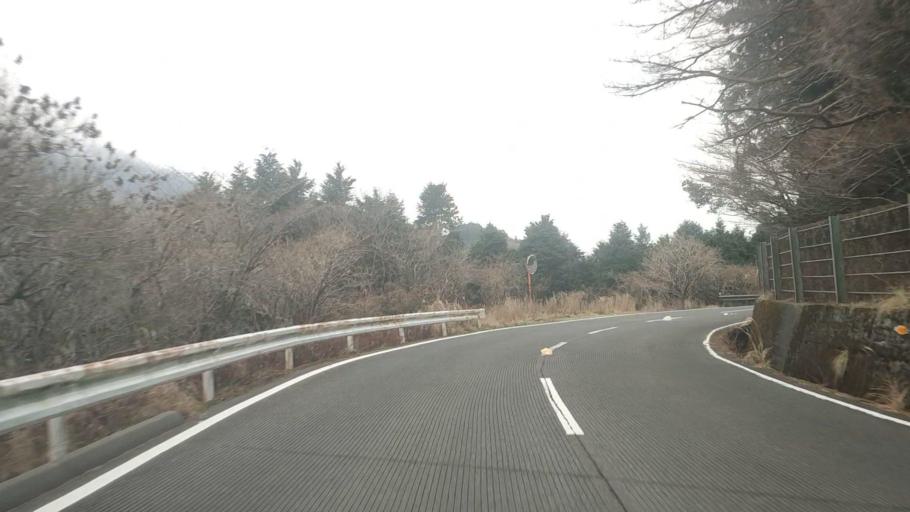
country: JP
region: Nagasaki
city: Shimabara
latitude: 32.7680
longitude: 130.2720
